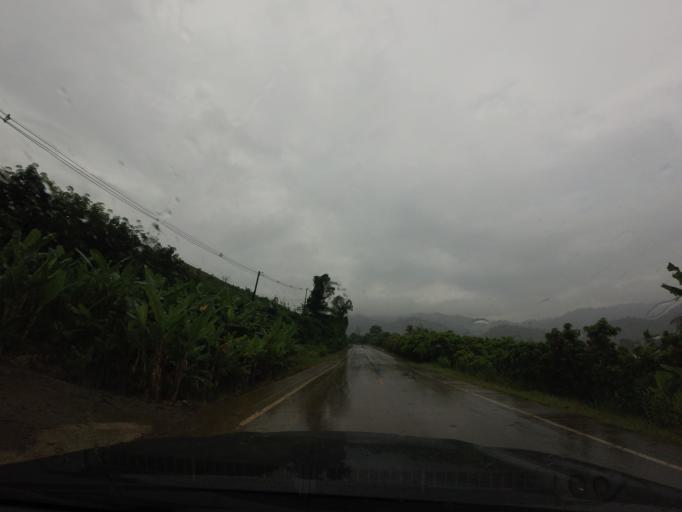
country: TH
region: Loei
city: Pak Chom
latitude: 18.1950
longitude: 102.0529
